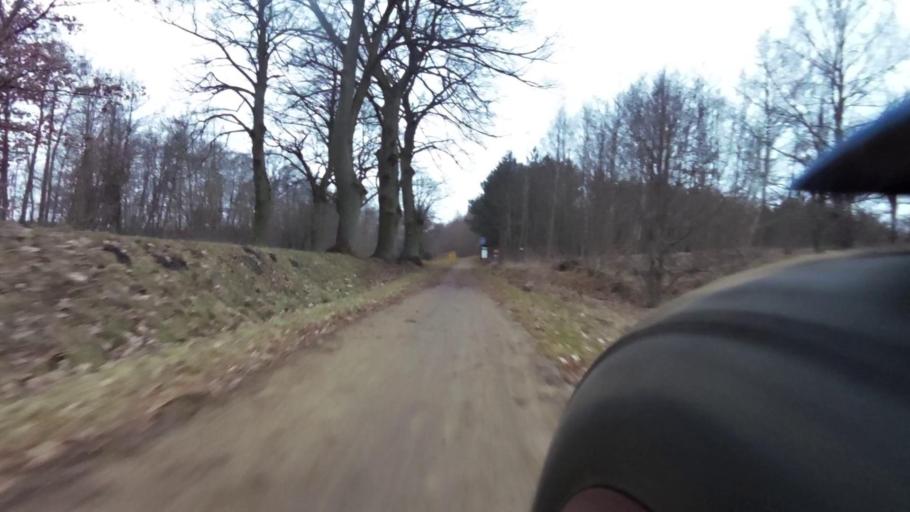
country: PL
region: West Pomeranian Voivodeship
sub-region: Powiat walecki
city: Walcz
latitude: 53.2438
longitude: 16.3735
